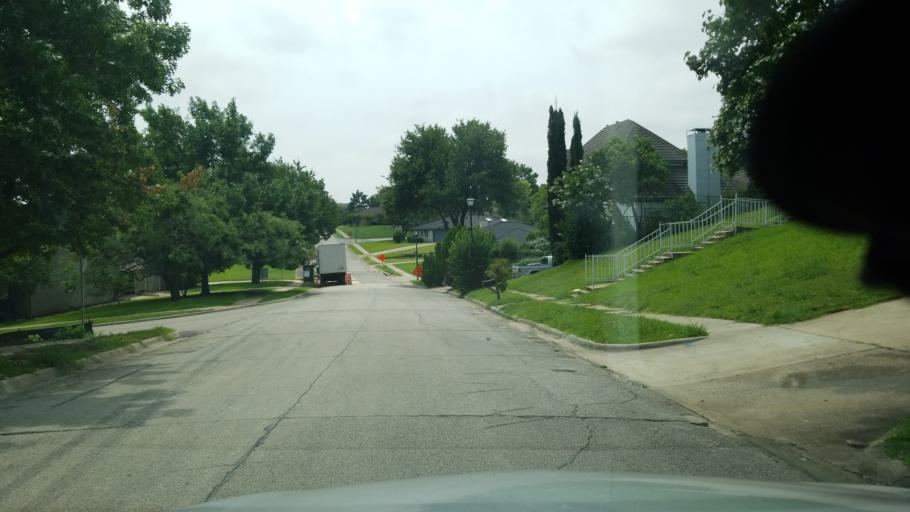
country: US
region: Texas
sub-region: Dallas County
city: Irving
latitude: 32.8556
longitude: -96.9398
